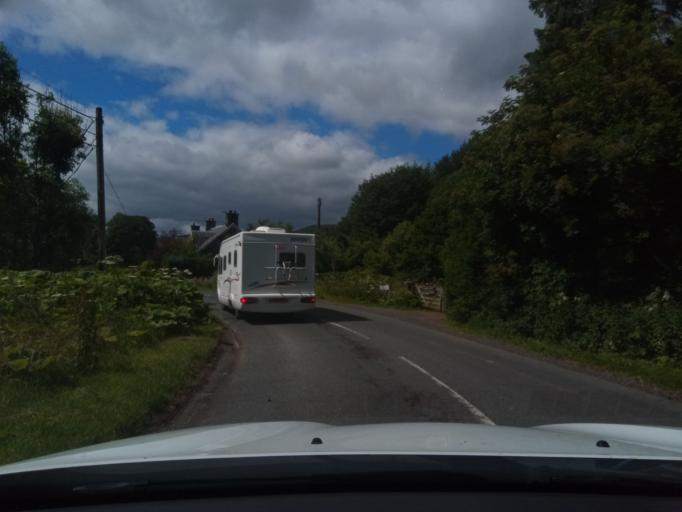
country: GB
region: Scotland
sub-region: The Scottish Borders
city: Innerleithen
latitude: 55.5413
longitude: -3.0150
